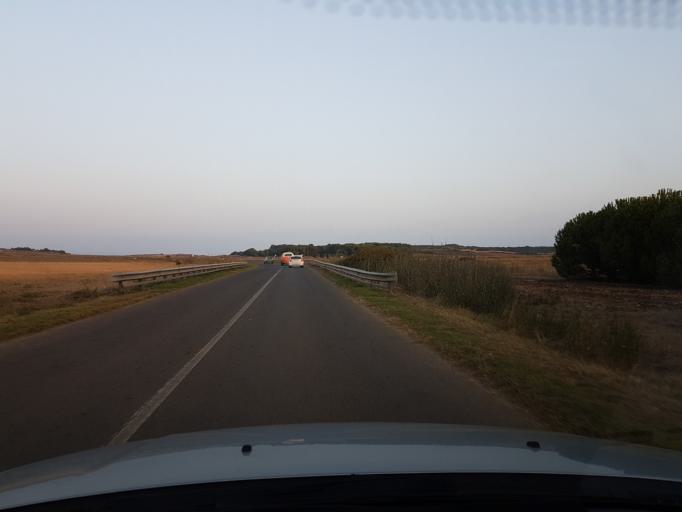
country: IT
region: Sardinia
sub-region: Provincia di Oristano
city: Cabras
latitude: 39.9420
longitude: 8.4374
